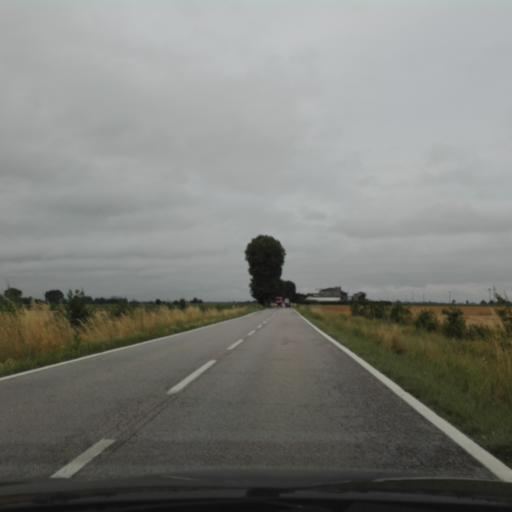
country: IT
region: Veneto
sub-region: Provincia di Padova
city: Barbona
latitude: 45.0785
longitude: 11.7223
